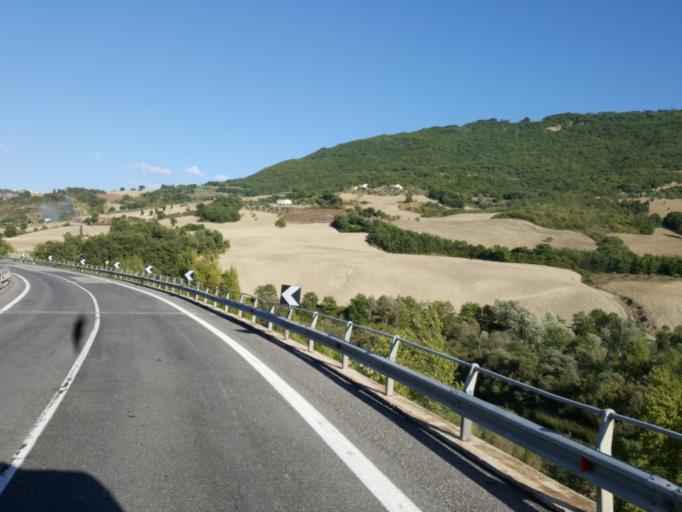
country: IT
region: Molise
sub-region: Provincia di Campobasso
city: Salcito
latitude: 41.7747
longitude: 14.5017
